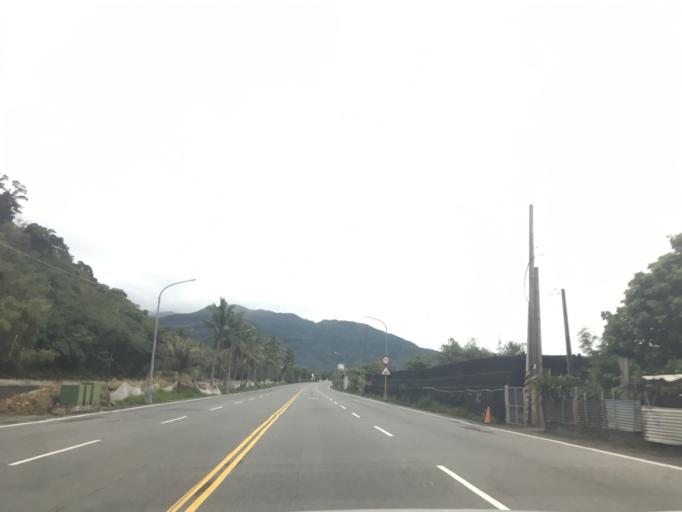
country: TW
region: Taiwan
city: Taitung City
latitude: 22.7422
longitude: 121.0573
